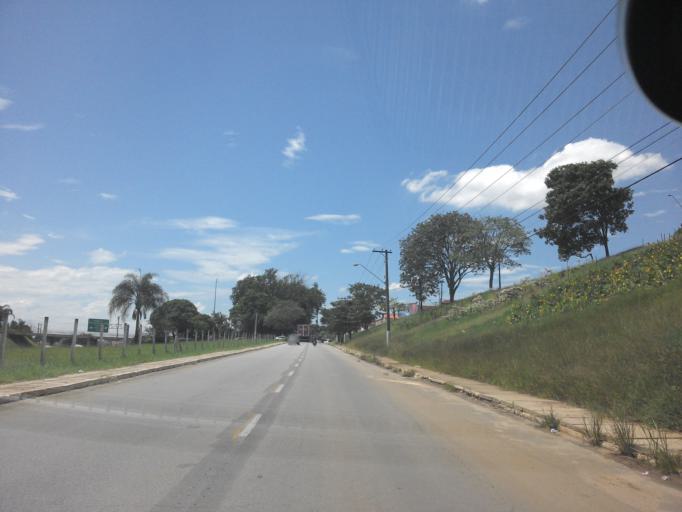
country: BR
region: Sao Paulo
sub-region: Taubate
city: Taubate
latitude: -23.0392
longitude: -45.5608
